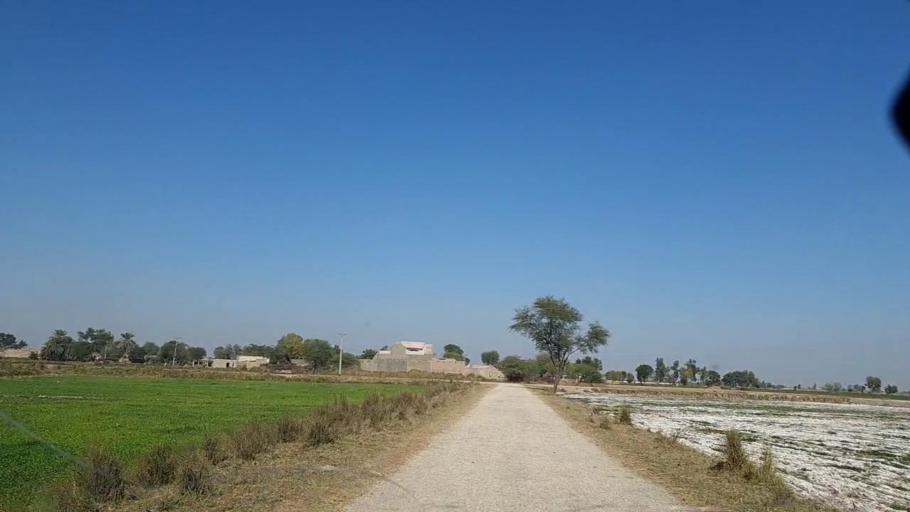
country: PK
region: Sindh
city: Khanpur
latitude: 27.8484
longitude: 69.3941
